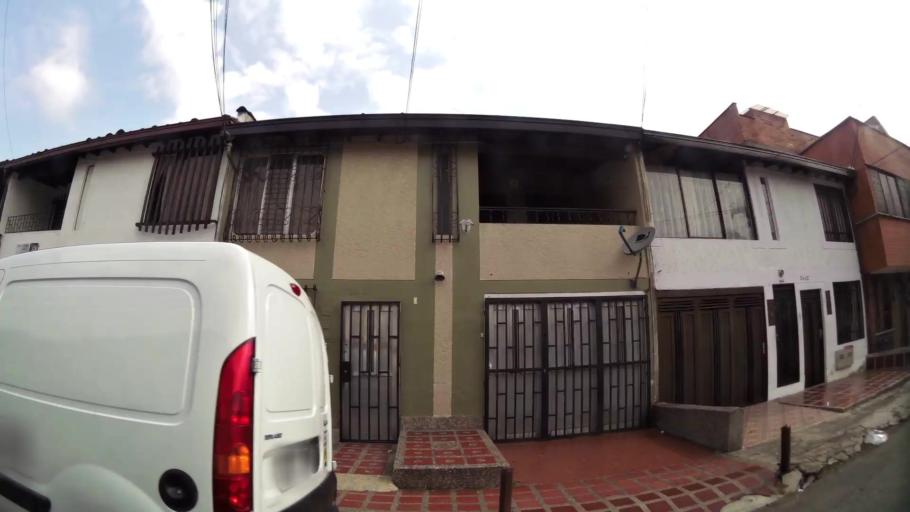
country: CO
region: Antioquia
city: Medellin
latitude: 6.2207
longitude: -75.5822
